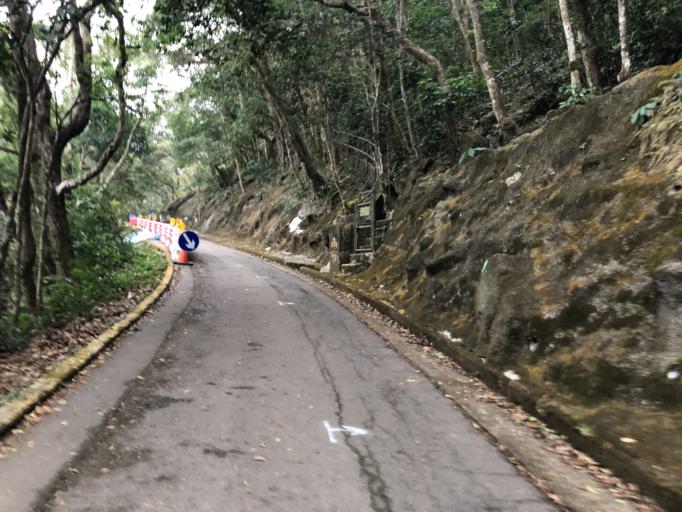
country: HK
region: Wanchai
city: Wan Chai
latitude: 22.2691
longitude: 114.2119
